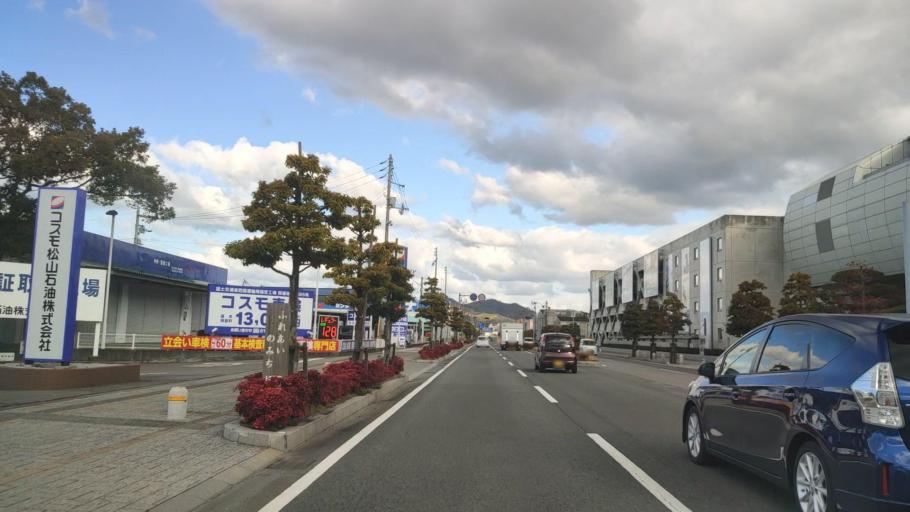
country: JP
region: Ehime
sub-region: Shikoku-chuo Shi
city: Matsuyama
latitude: 33.8499
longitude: 132.7133
